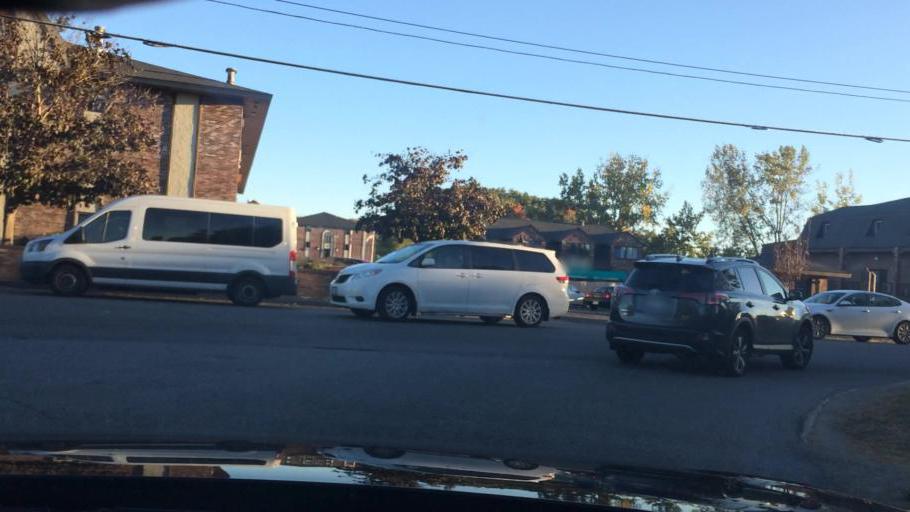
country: US
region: Massachusetts
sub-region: Middlesex County
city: Chelmsford
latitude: 42.6267
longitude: -71.3586
